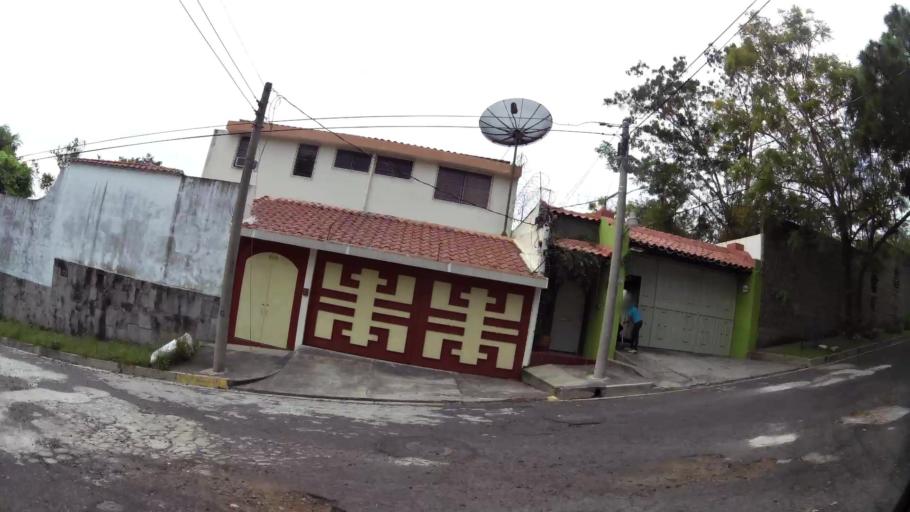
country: SV
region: San Salvador
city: Mejicanos
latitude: 13.7201
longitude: -89.2447
